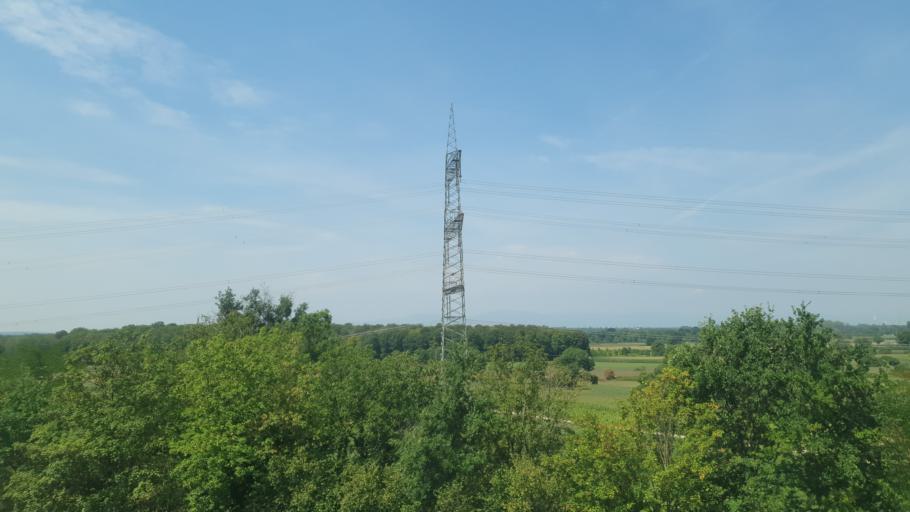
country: DE
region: Baden-Wuerttemberg
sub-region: Freiburg Region
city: Schliengen
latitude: 47.7538
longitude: 7.5639
